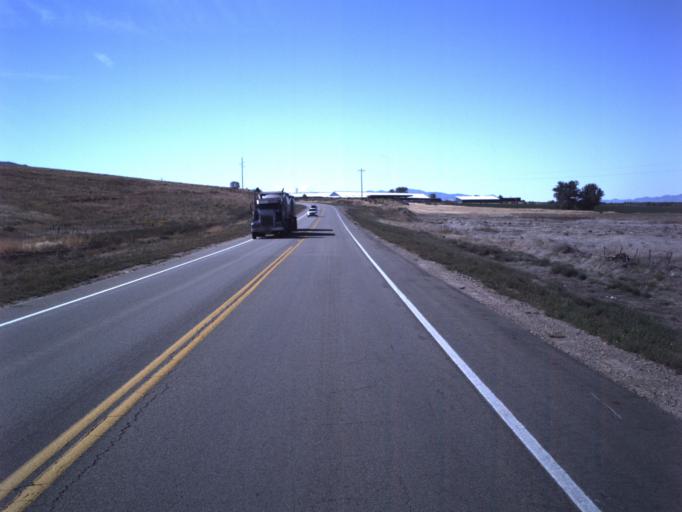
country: US
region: Utah
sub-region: Juab County
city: Nephi
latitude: 39.5286
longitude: -111.8652
